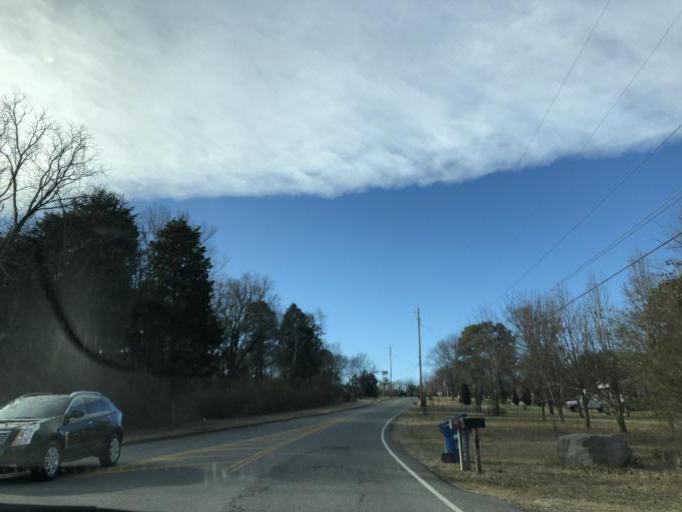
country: US
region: Tennessee
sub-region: Wilson County
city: Green Hill
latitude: 36.1577
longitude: -86.5790
